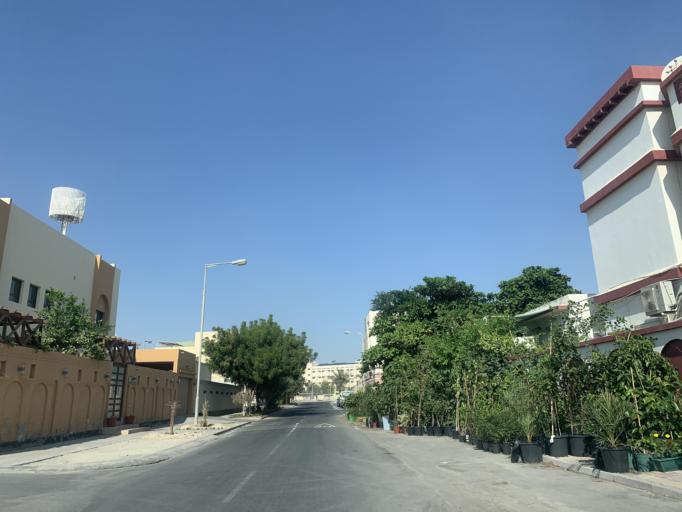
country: BH
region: Central Governorate
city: Madinat Hamad
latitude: 26.1209
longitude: 50.4944
